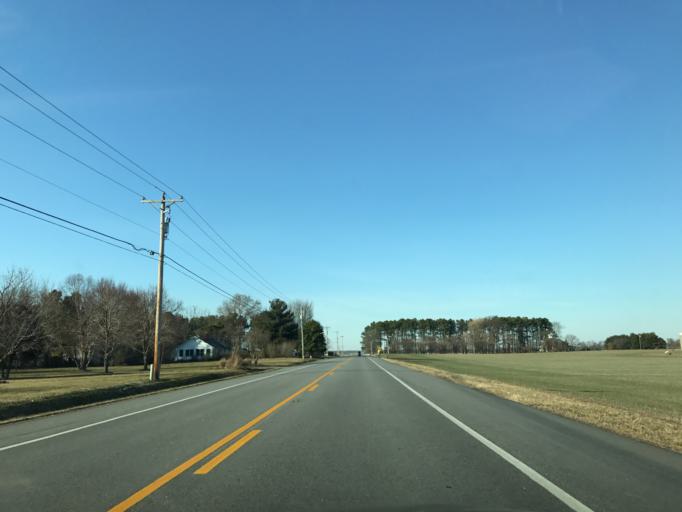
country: US
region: Maryland
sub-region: Queen Anne's County
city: Kingstown
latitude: 39.1991
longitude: -75.8623
